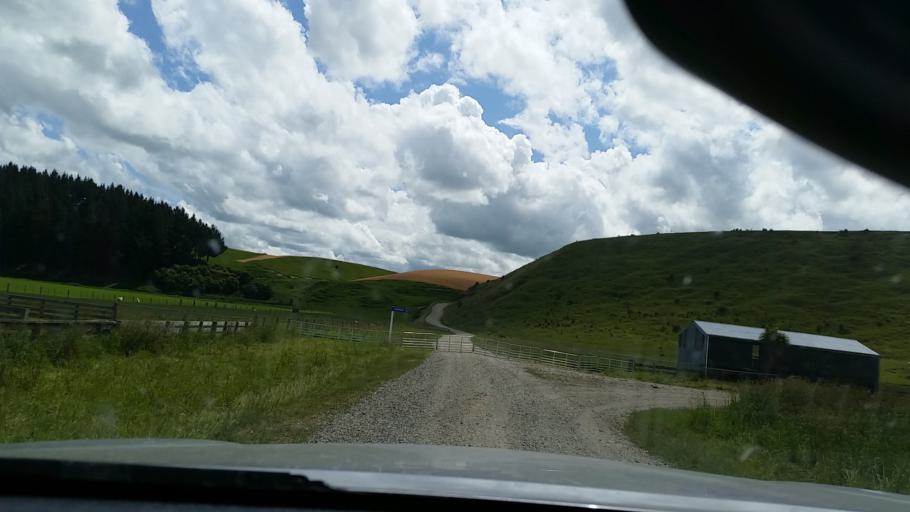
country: NZ
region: Southland
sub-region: Gore District
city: Gore
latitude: -45.7838
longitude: 168.7810
